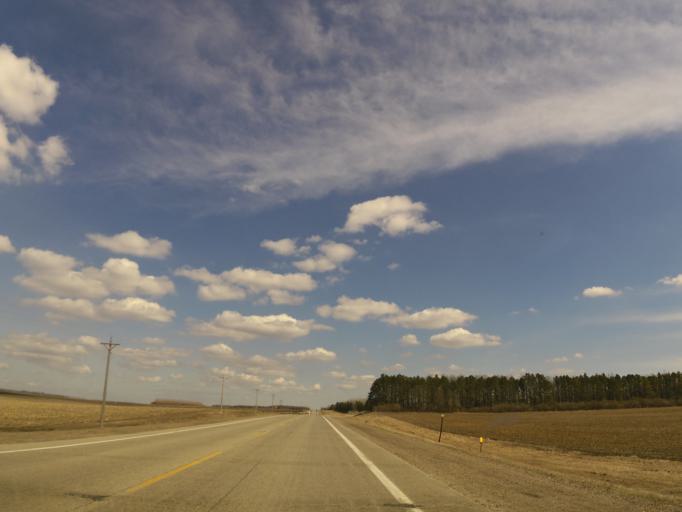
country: US
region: South Dakota
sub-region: Codington County
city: Watertown
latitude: 44.8900
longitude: -96.9624
